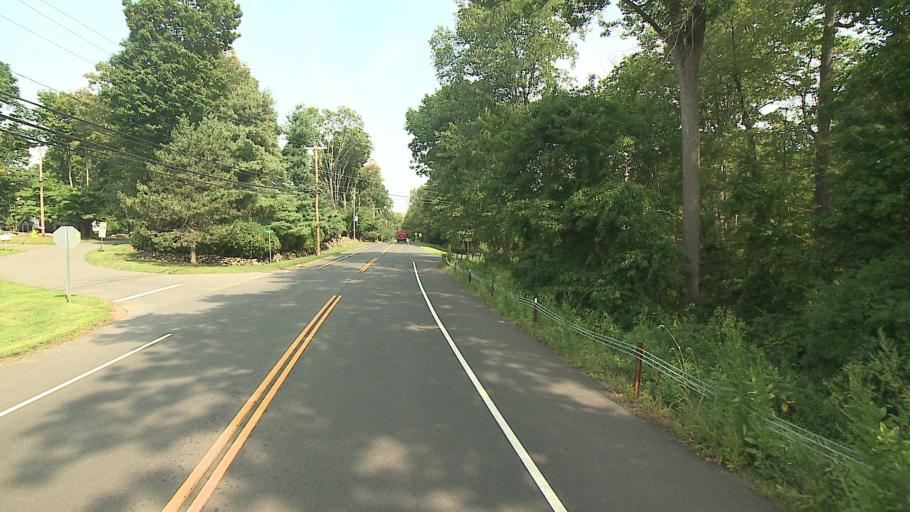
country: US
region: Connecticut
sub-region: Fairfield County
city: Bethel
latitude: 41.3115
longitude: -73.3849
